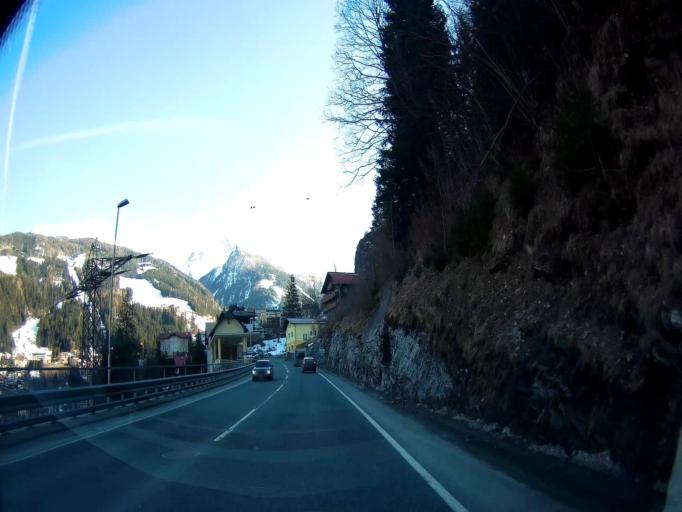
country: AT
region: Salzburg
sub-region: Politischer Bezirk Sankt Johann im Pongau
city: Bad Gastein
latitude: 47.1223
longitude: 13.1315
